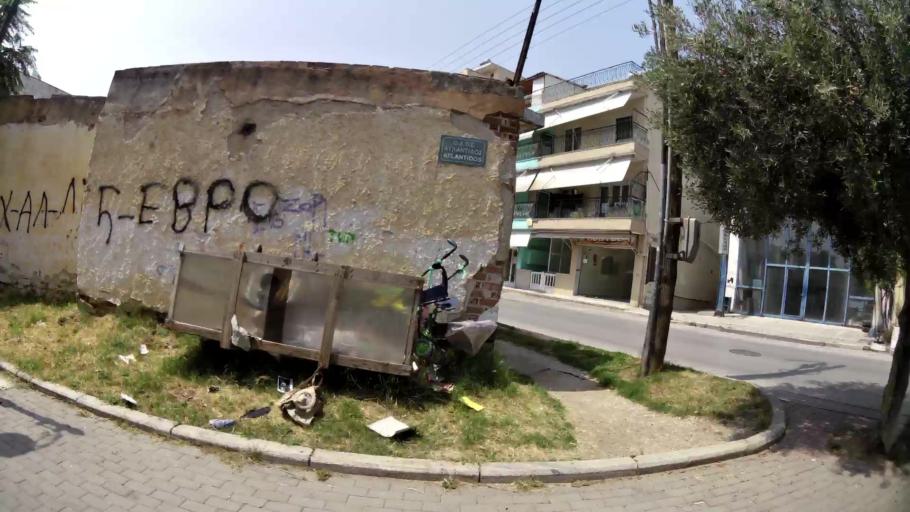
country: GR
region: Central Macedonia
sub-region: Nomos Thessalonikis
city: Evosmos
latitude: 40.6627
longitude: 22.9085
